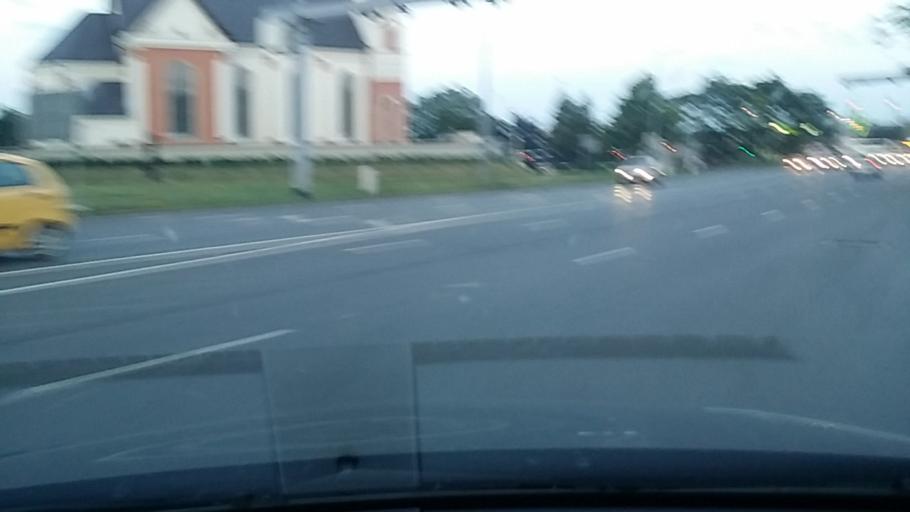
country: HU
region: Borsod-Abauj-Zemplen
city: Miskolc
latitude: 48.1068
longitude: 20.7893
